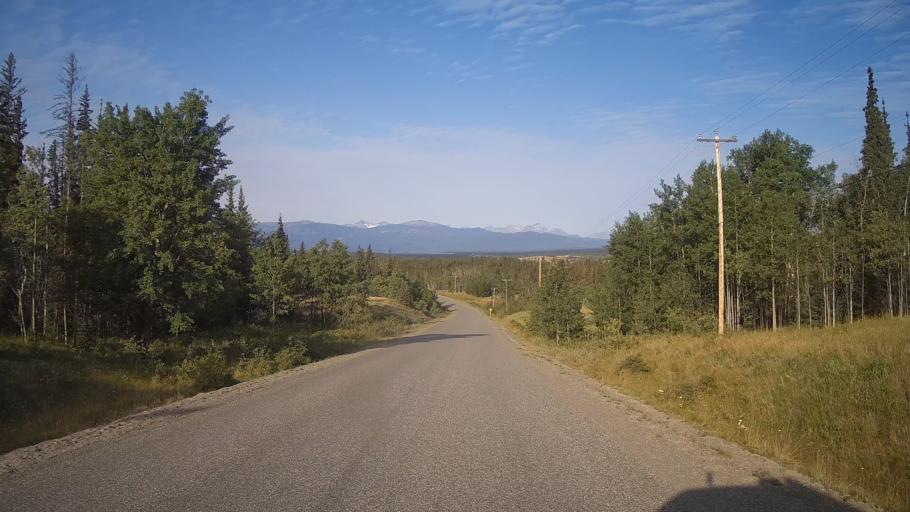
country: CA
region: British Columbia
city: Hanceville
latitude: 51.9497
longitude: -124.4501
